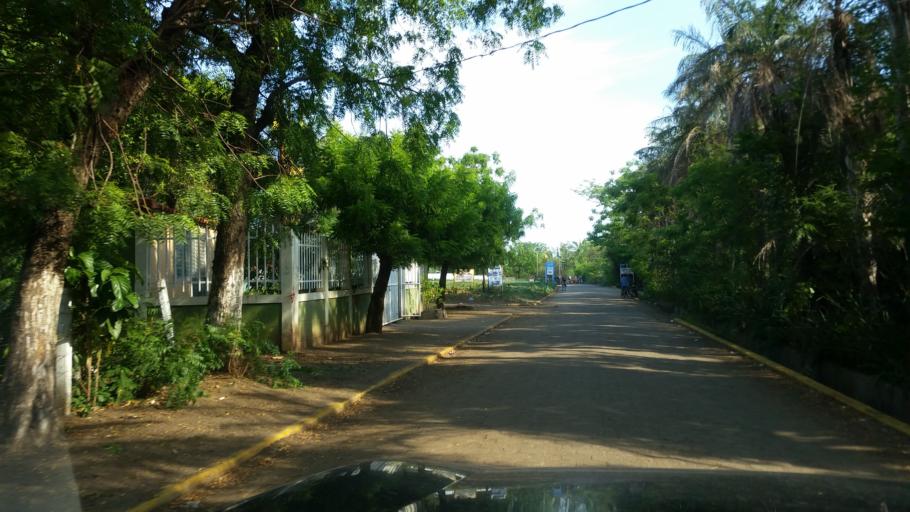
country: NI
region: Managua
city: Masachapa
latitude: 11.7805
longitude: -86.5167
